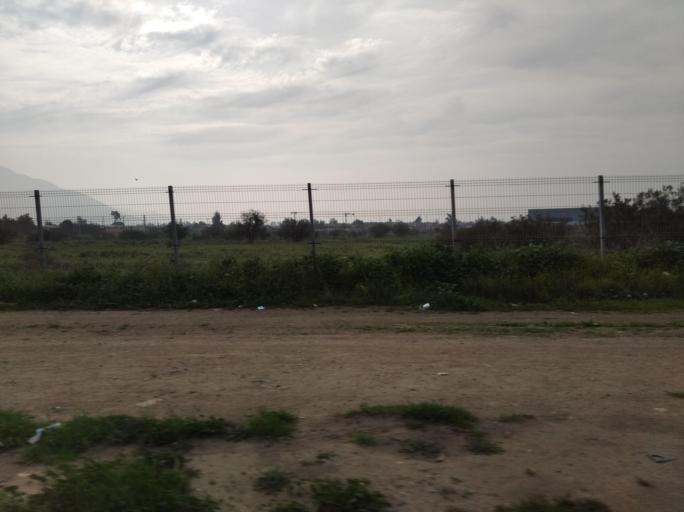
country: CL
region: Santiago Metropolitan
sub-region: Provincia de Chacabuco
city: Lampa
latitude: -33.2938
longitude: -70.8812
